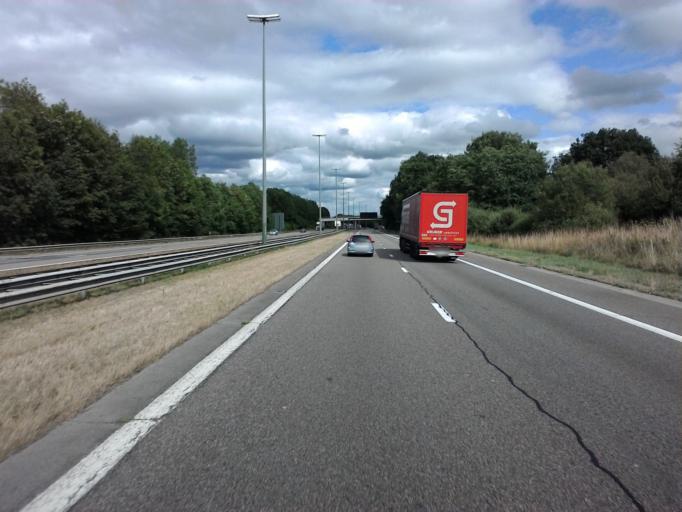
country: BE
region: Wallonia
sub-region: Province du Luxembourg
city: Arlon
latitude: 49.6691
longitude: 5.7937
